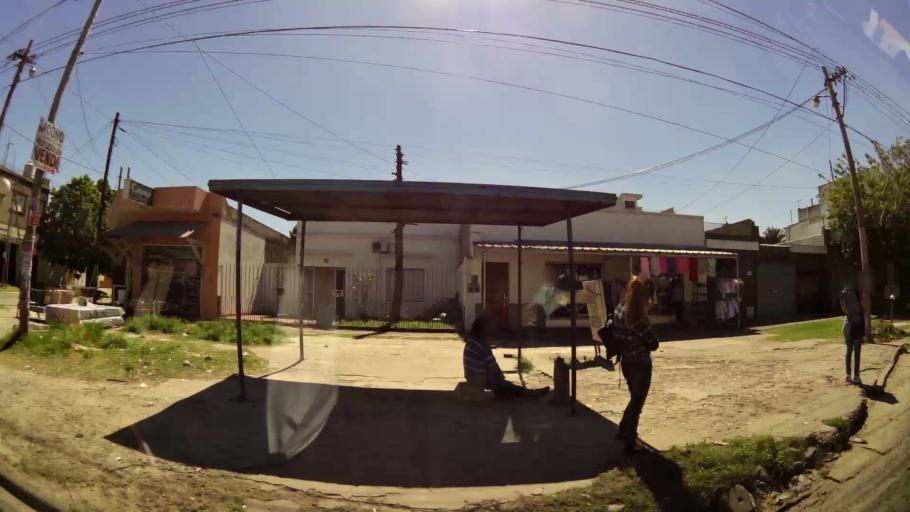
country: AR
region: Buenos Aires
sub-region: Partido de Quilmes
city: Quilmes
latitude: -34.7138
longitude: -58.3073
